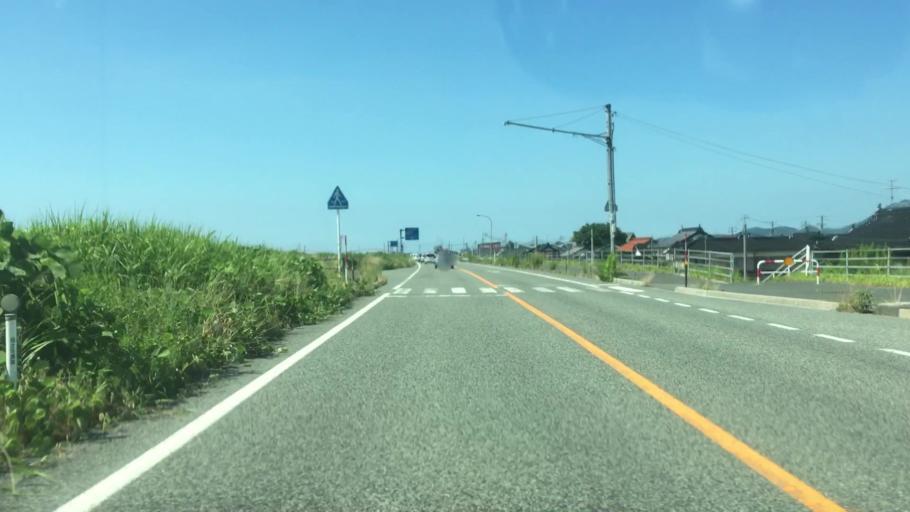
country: JP
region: Tottori
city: Tottori
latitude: 35.4604
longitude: 134.2151
